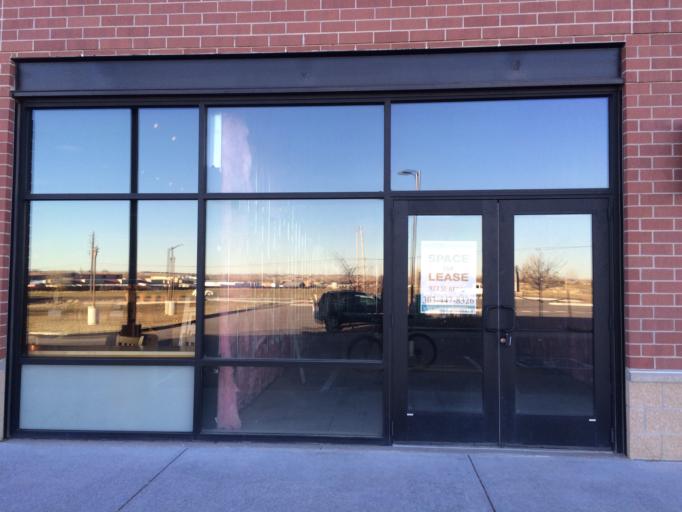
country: US
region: Colorado
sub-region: Boulder County
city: Louisville
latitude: 39.9801
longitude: -105.1289
